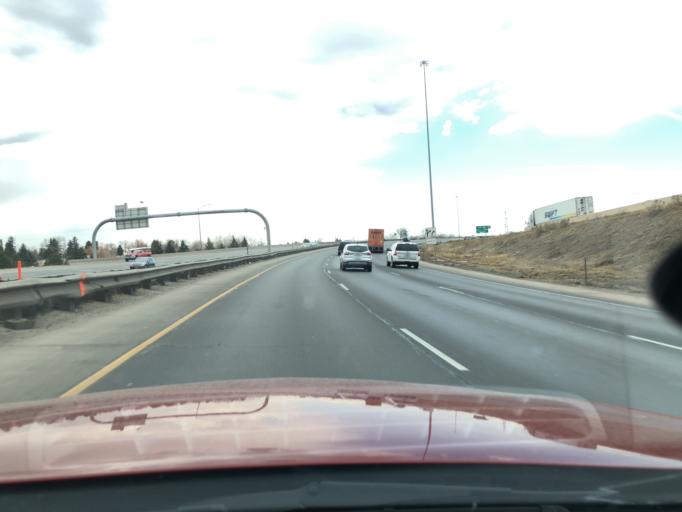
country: US
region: Colorado
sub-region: Jefferson County
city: Applewood
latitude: 39.7758
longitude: -105.1430
